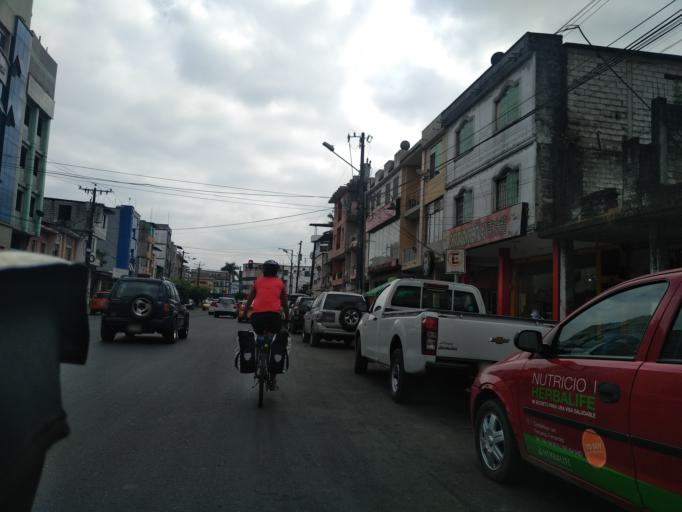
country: EC
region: Los Rios
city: Quevedo
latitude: -1.0308
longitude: -79.4694
